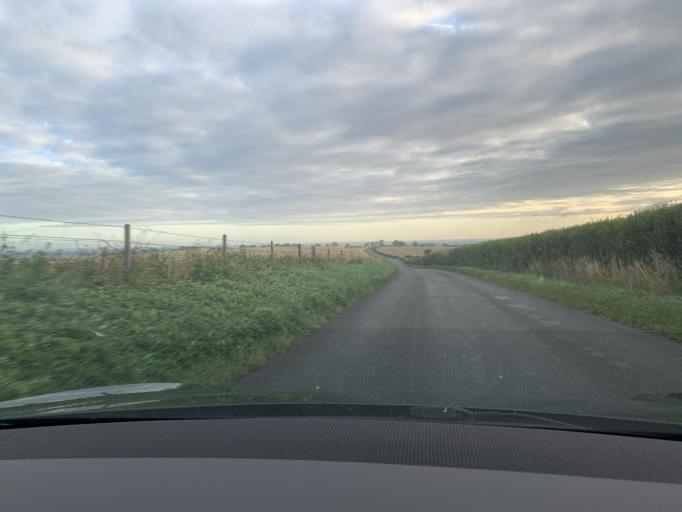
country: GB
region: England
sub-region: Wiltshire
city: Collingbourne Kingston
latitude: 51.3209
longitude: -1.6197
